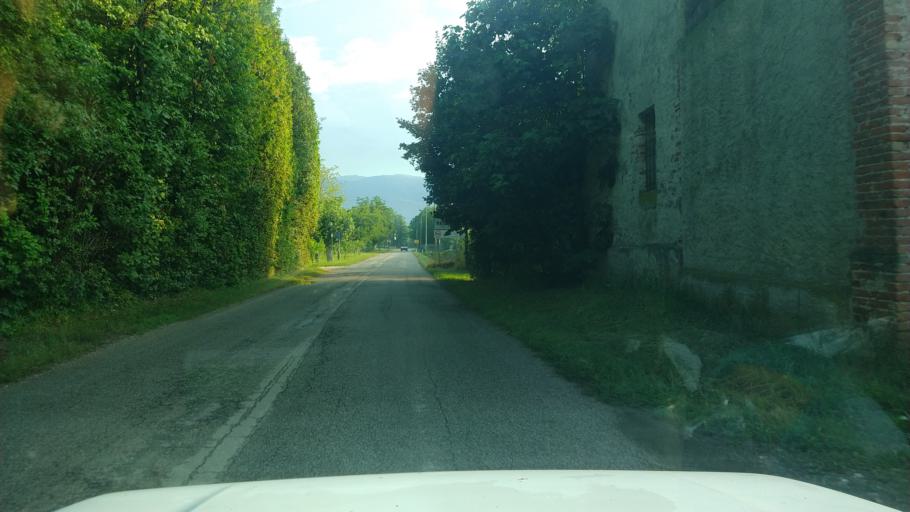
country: IT
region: Veneto
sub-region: Provincia di Vicenza
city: Nove
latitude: 45.7203
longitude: 11.6578
